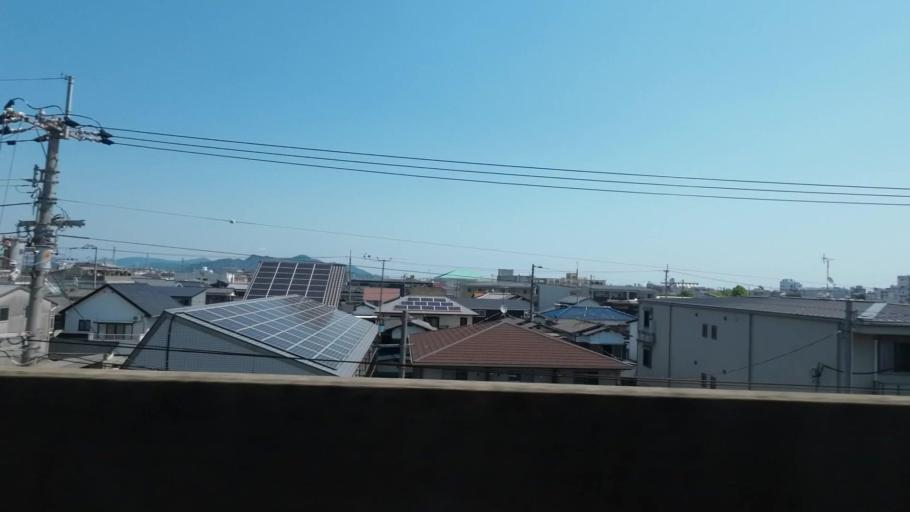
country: JP
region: Ehime
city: Hojo
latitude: 34.0699
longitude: 132.9885
